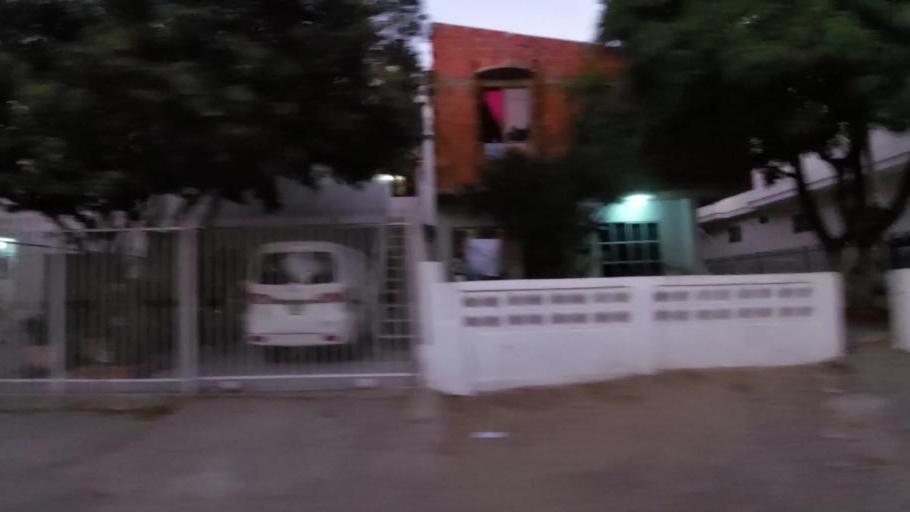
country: CO
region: Bolivar
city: Cartagena
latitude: 10.3867
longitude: -75.4941
